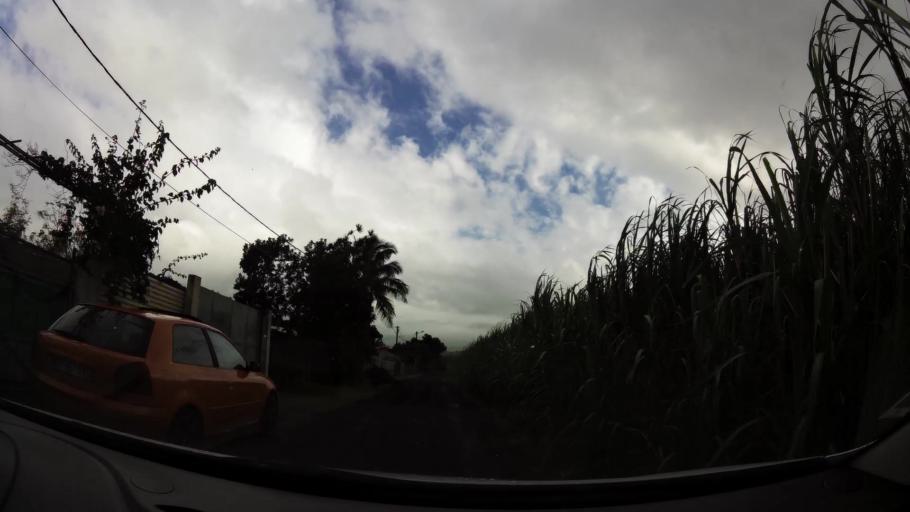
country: RE
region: Reunion
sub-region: Reunion
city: Saint-Andre
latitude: -20.9274
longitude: 55.6445
